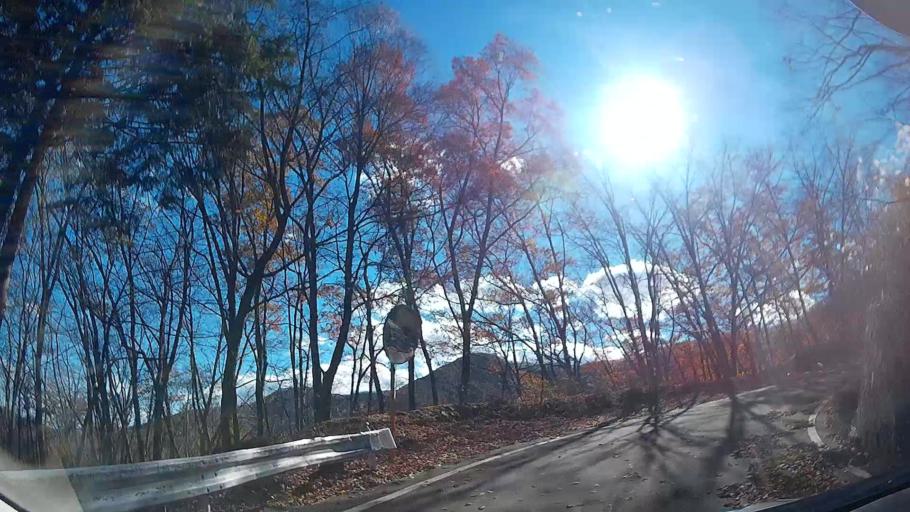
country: JP
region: Yamanashi
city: Otsuki
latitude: 35.7361
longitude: 138.9522
